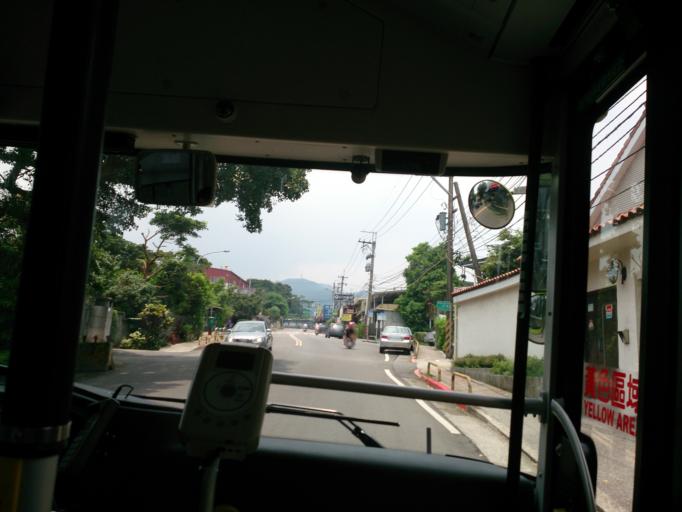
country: TW
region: Taipei
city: Taipei
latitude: 25.1174
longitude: 121.5518
